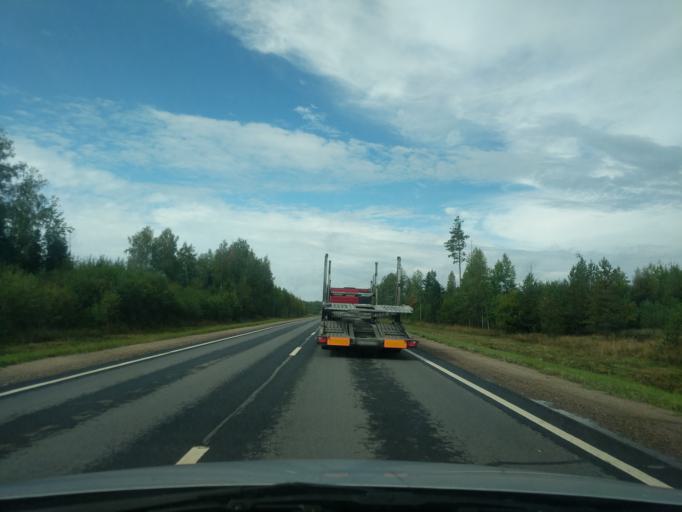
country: RU
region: Kostroma
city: Sudislavl'
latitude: 57.8245
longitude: 41.8966
